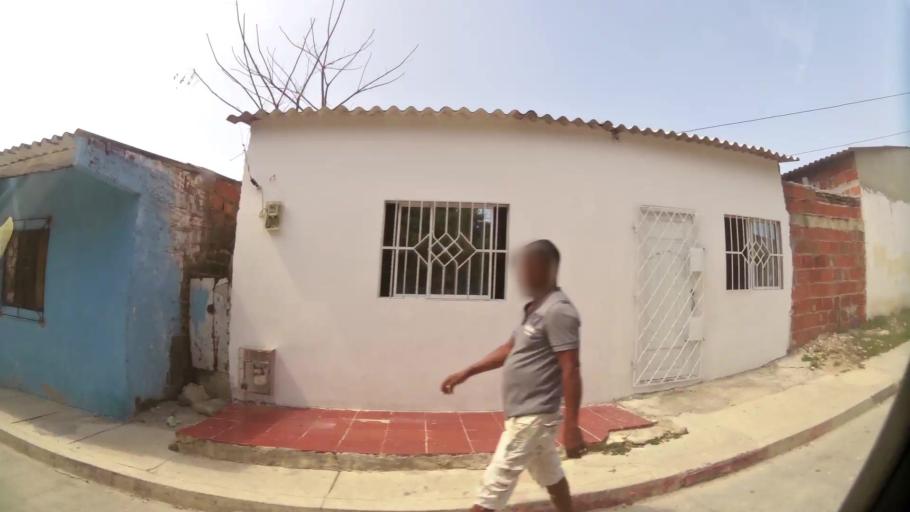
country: CO
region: Atlantico
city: Barranquilla
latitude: 10.9620
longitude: -74.8261
